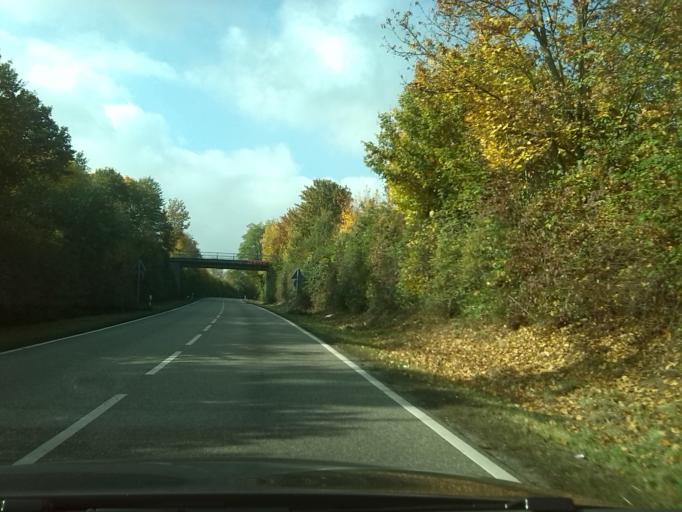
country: DE
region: Baden-Wuerttemberg
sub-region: Regierungsbezirk Stuttgart
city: Stuttgart Muehlhausen
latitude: 48.8594
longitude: 9.2470
